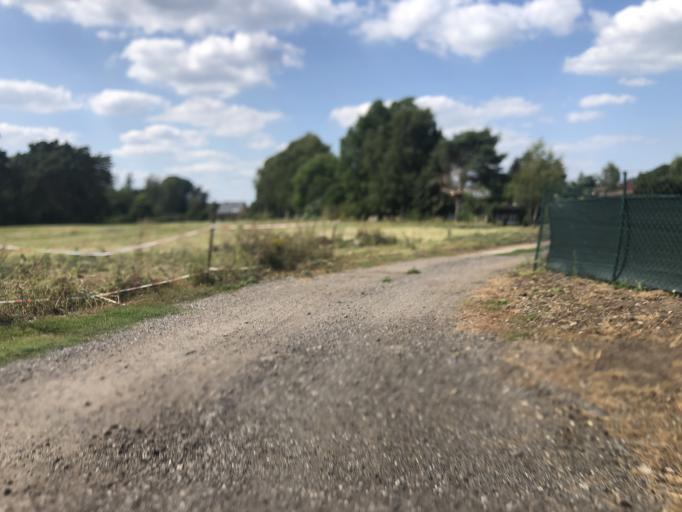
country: DE
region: Brandenburg
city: Mullrose
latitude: 52.2362
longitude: 14.4118
